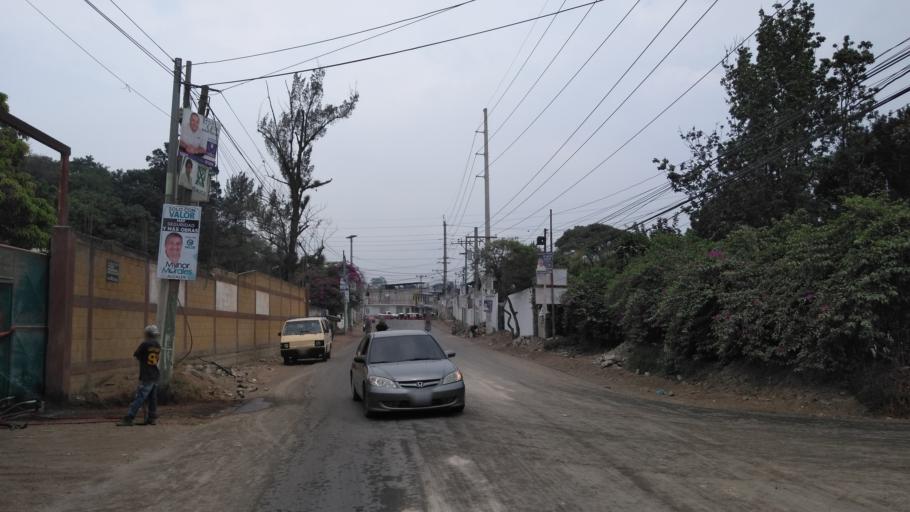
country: GT
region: Guatemala
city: Petapa
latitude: 14.5096
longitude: -90.5568
